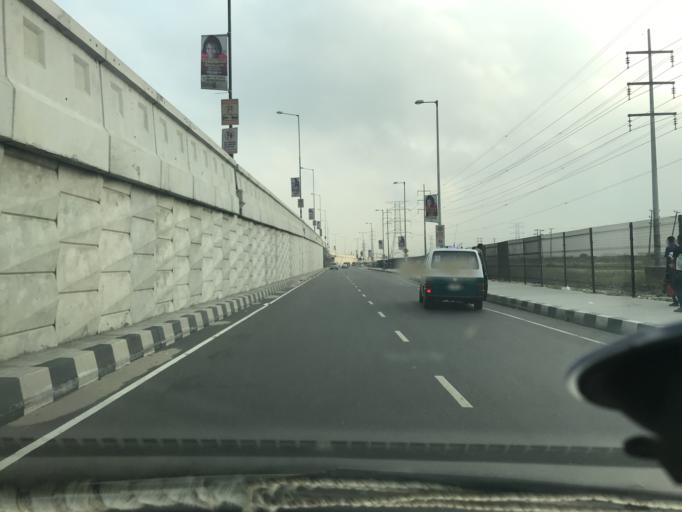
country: NG
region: Lagos
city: Ikoyi
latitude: 6.4668
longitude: 3.5637
